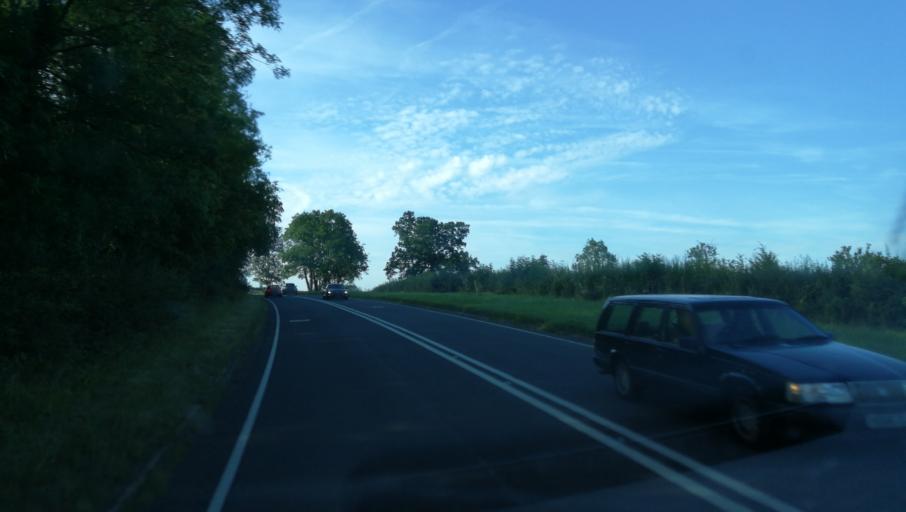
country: GB
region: England
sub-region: Oxfordshire
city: Deddington
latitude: 51.9657
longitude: -1.3206
